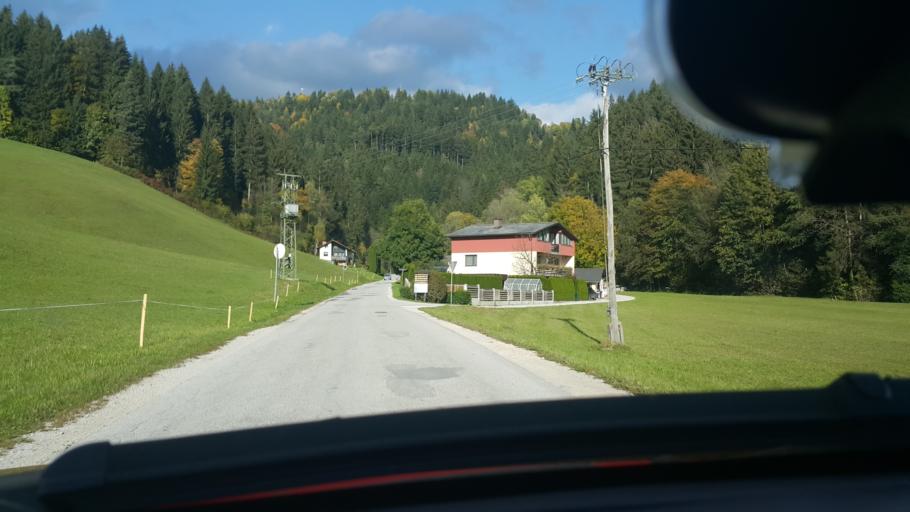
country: SI
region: Vitanje
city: Vitanje
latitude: 46.3911
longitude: 15.3074
